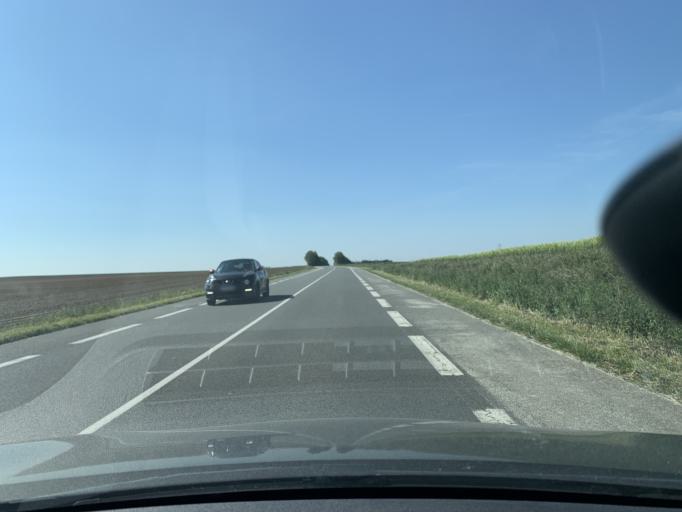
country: FR
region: Nord-Pas-de-Calais
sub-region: Departement du Nord
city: Rumilly-en-Cambresis
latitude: 50.1205
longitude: 3.2460
